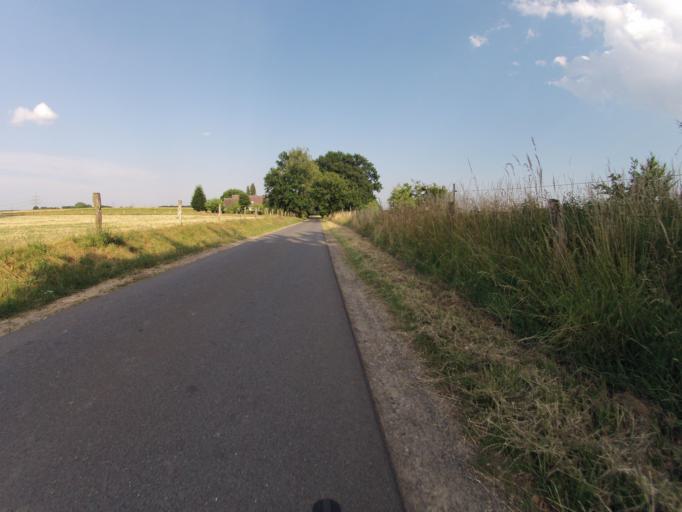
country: DE
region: North Rhine-Westphalia
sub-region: Regierungsbezirk Munster
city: Tecklenburg
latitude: 52.2716
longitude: 7.8342
